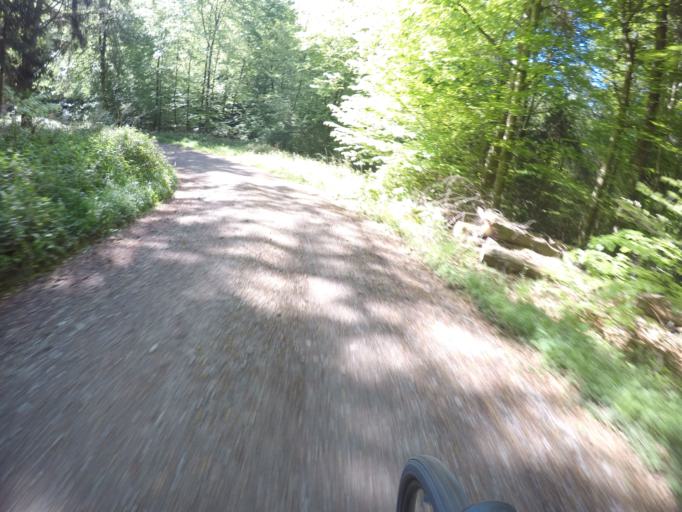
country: DE
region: Baden-Wuerttemberg
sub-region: Tuebingen Region
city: Dettenhausen
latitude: 48.5889
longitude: 9.1007
